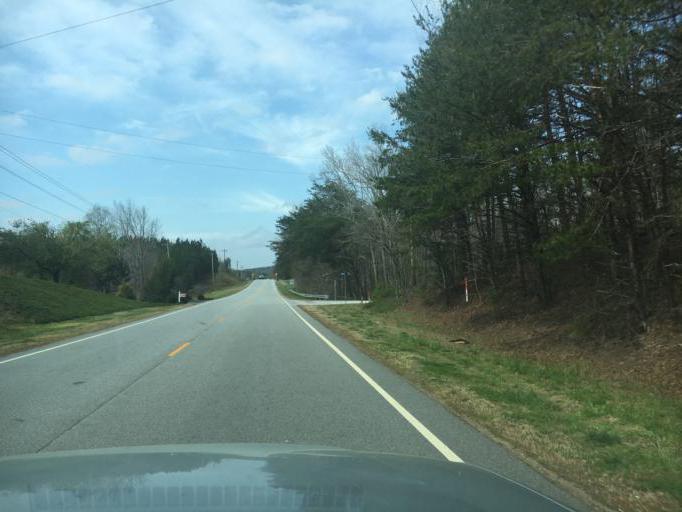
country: US
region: South Carolina
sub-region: Greenville County
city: Tigerville
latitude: 35.1216
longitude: -82.3300
